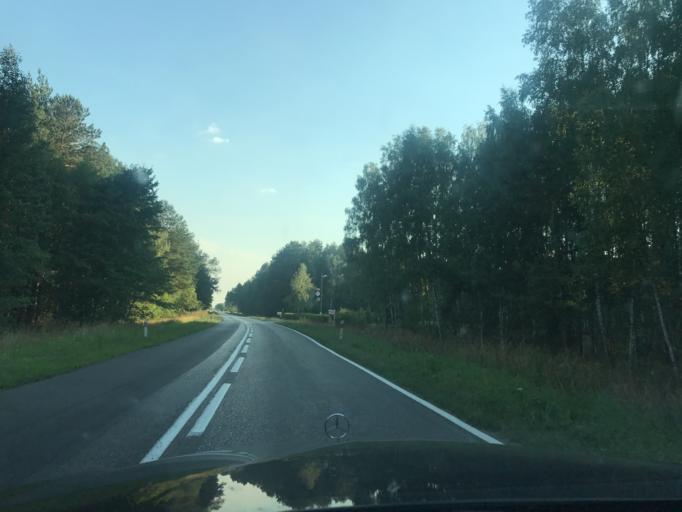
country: PL
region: Lublin Voivodeship
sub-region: Powiat parczewski
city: Jablon
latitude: 51.6938
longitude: 23.0384
